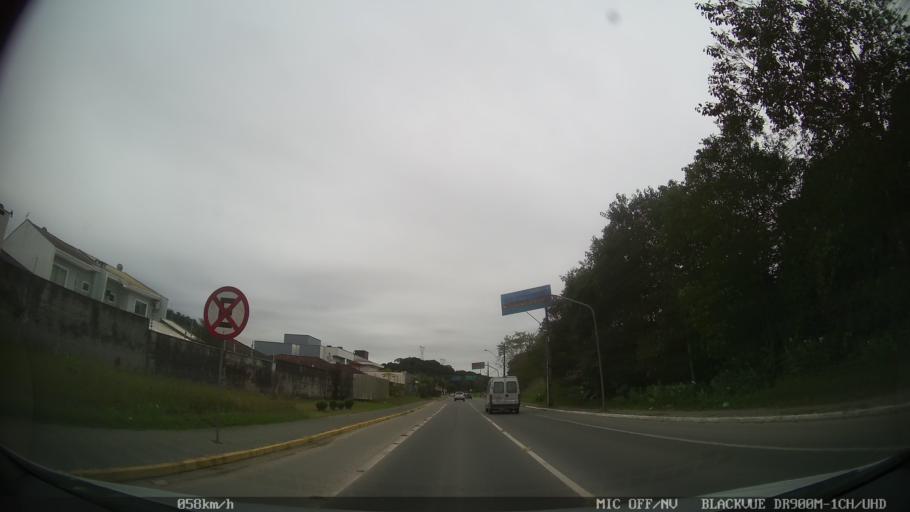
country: BR
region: Santa Catarina
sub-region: Joinville
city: Joinville
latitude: -26.2917
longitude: -48.8936
